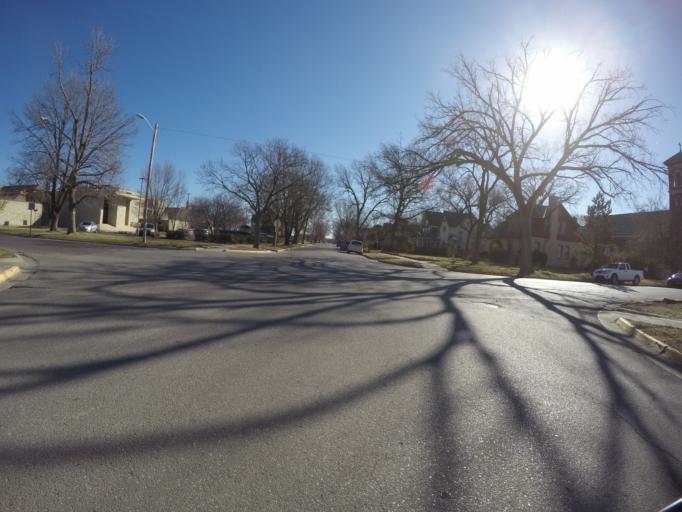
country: US
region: Kansas
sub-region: Riley County
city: Manhattan
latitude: 39.1783
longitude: -96.5670
